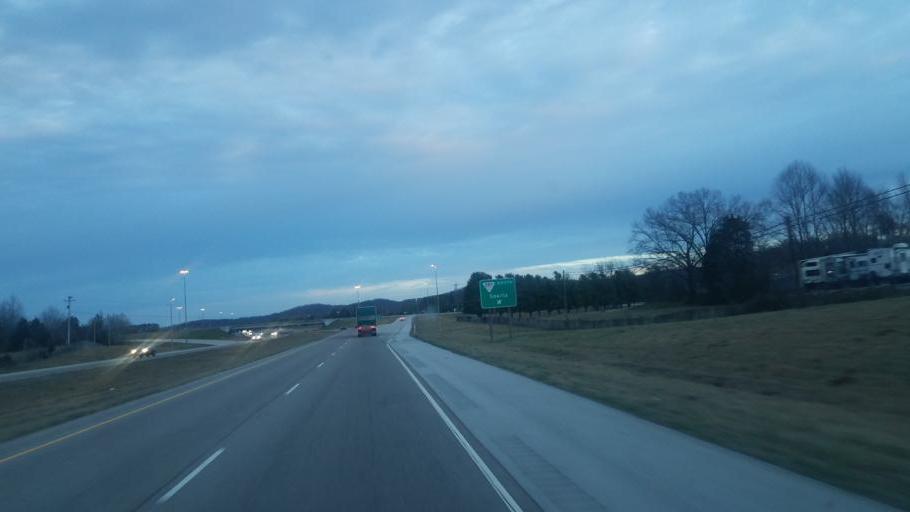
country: US
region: Tennessee
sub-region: White County
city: Sparta
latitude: 35.9611
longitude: -85.4857
